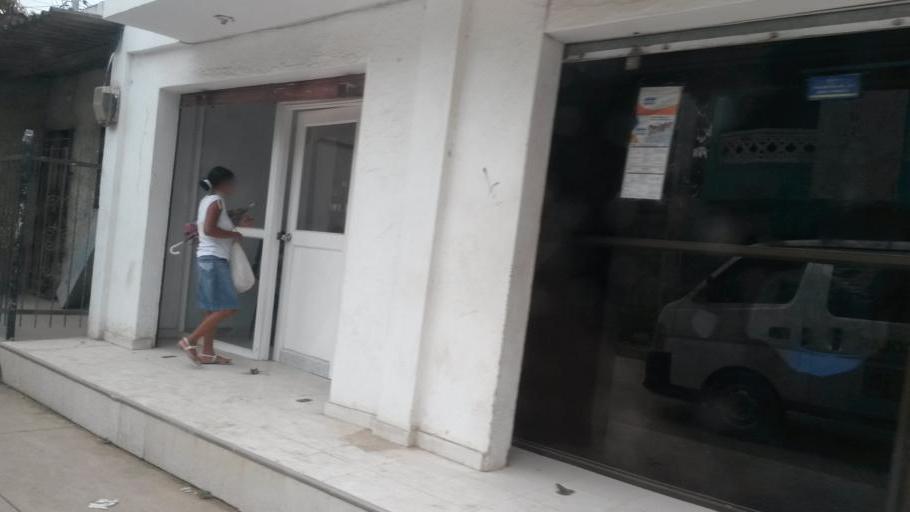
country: CO
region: Bolivar
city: Cartagena
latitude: 10.4066
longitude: -75.4545
